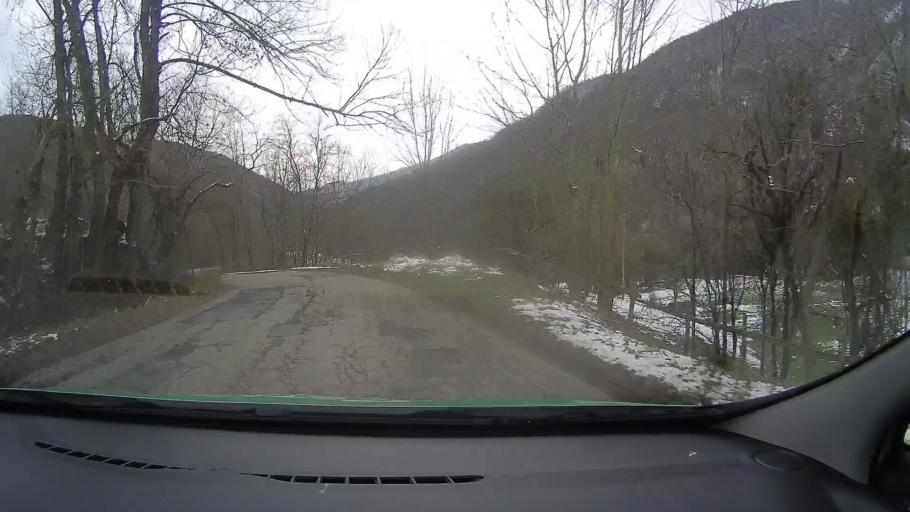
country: RO
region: Hunedoara
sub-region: Comuna Balsa
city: Balsa
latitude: 46.0166
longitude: 23.1488
